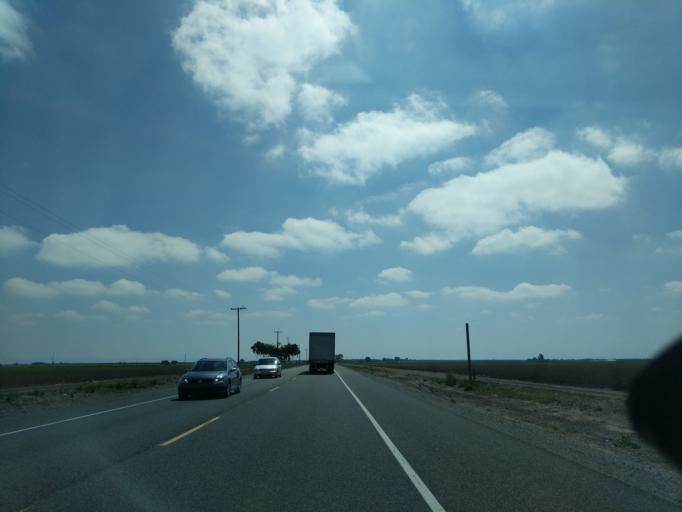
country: US
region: California
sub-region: San Joaquin County
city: Linden
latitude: 37.9420
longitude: -121.1187
